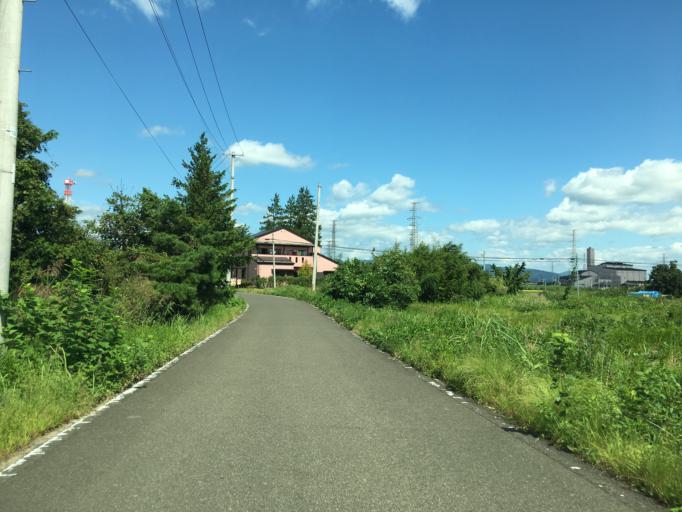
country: JP
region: Fukushima
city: Fukushima-shi
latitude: 37.7458
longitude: 140.4199
